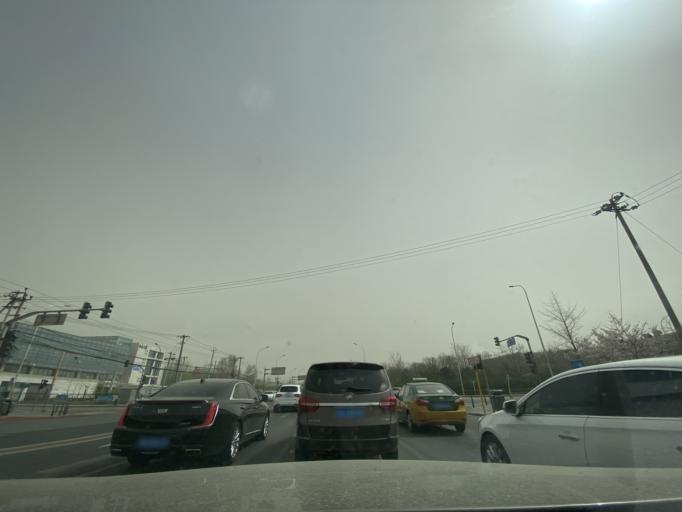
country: CN
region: Beijing
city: Sijiqing
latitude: 39.9457
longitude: 116.2622
